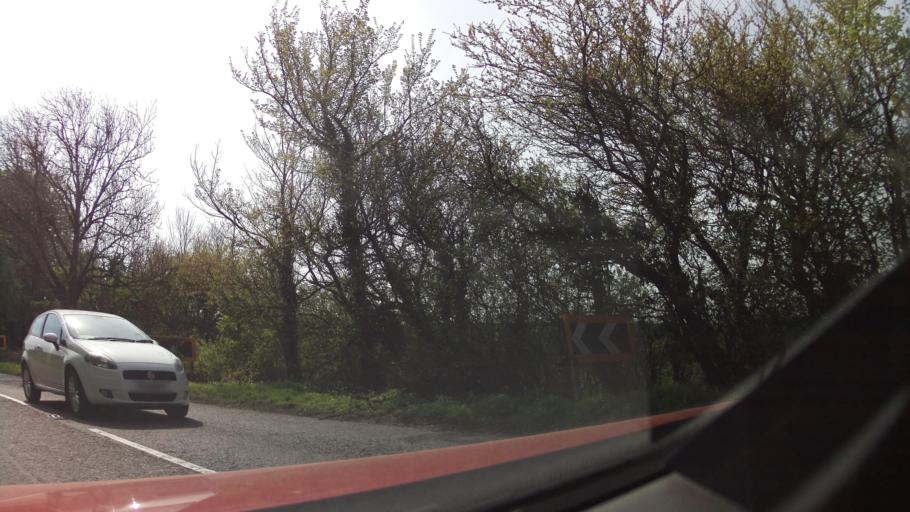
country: GB
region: England
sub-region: Somerset
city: Ilchester
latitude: 51.0269
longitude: -2.6913
